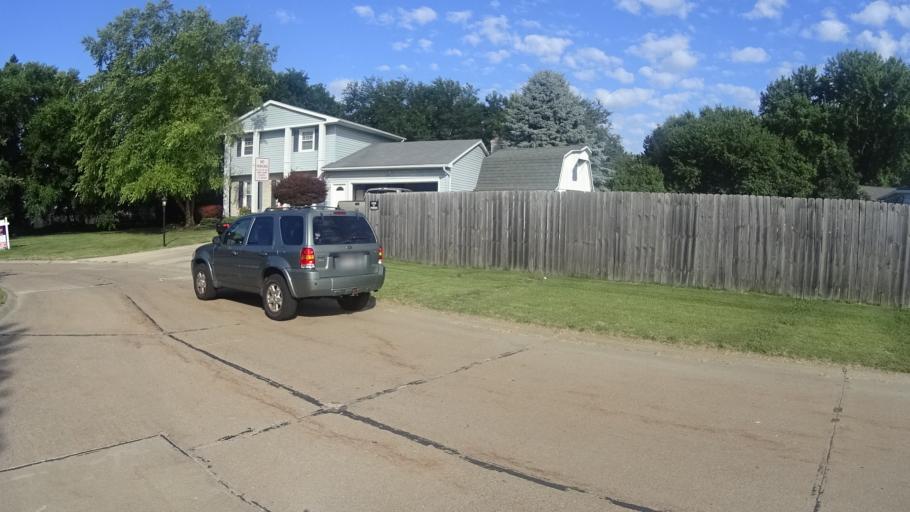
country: US
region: Ohio
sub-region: Erie County
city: Sandusky
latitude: 41.4269
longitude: -82.6796
